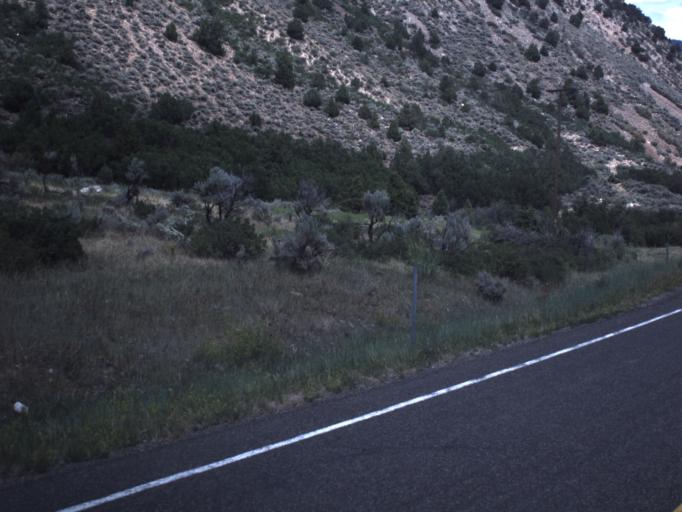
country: US
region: Utah
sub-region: Summit County
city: Francis
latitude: 40.4566
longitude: -110.8521
